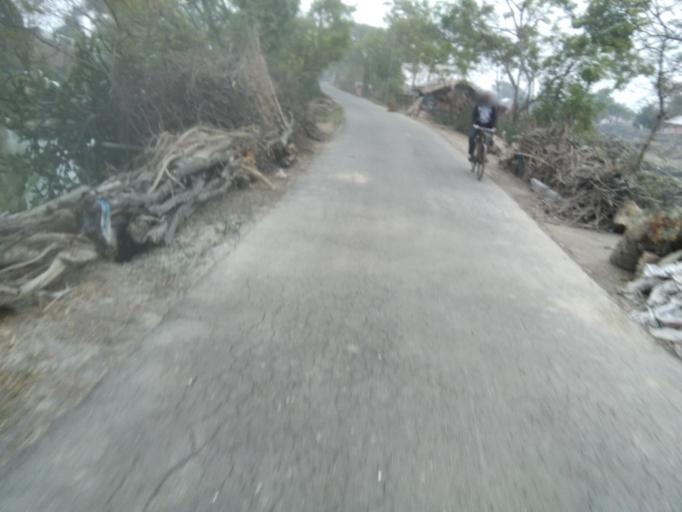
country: BD
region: Khulna
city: Satkhira
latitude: 22.5773
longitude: 89.0730
